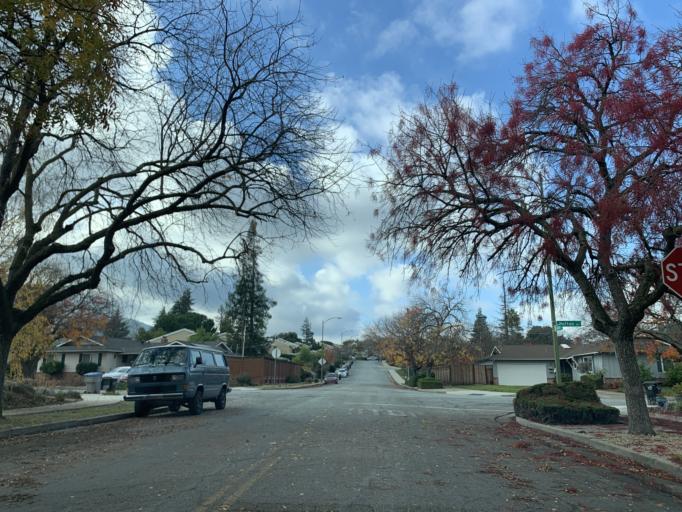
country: US
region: California
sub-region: Santa Clara County
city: Cambrian Park
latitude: 37.2446
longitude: -121.9087
